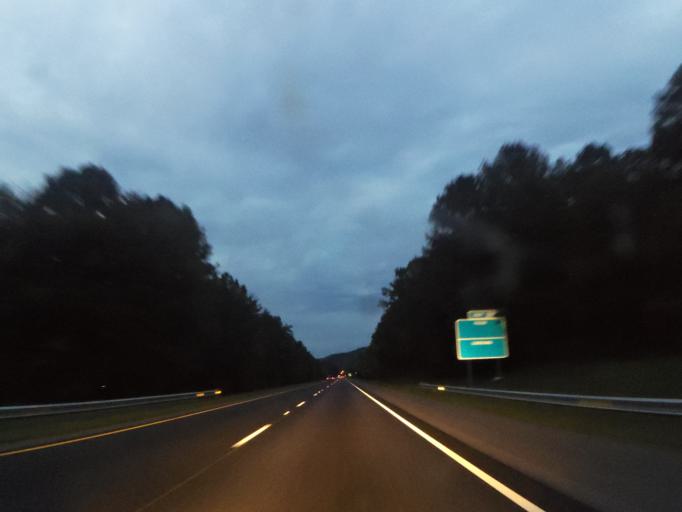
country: US
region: Alabama
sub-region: DeKalb County
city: Collinsville
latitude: 34.2663
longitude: -85.8876
